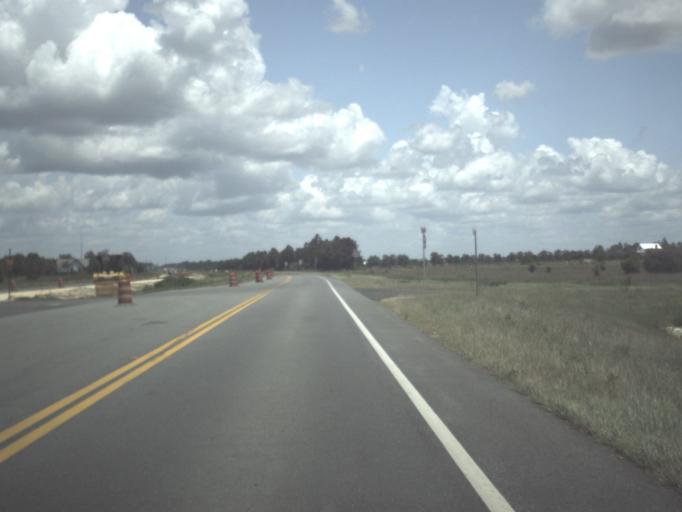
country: US
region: Florida
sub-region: Walton County
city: Freeport
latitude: 30.5514
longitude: -86.1062
